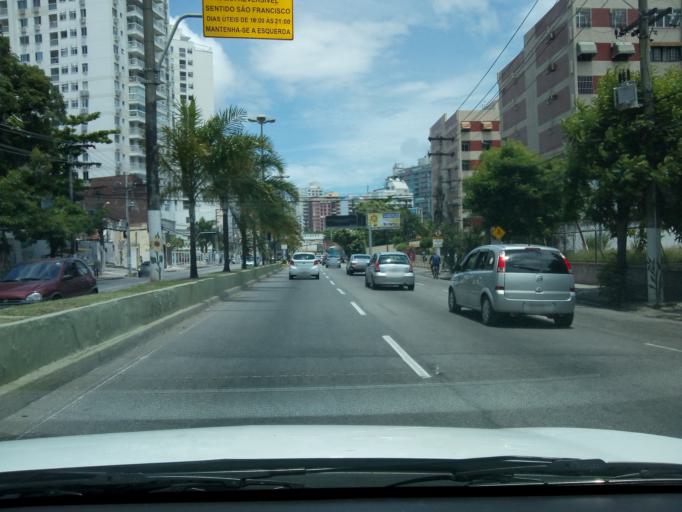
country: BR
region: Rio de Janeiro
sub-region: Niteroi
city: Niteroi
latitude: -22.8972
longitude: -43.1121
